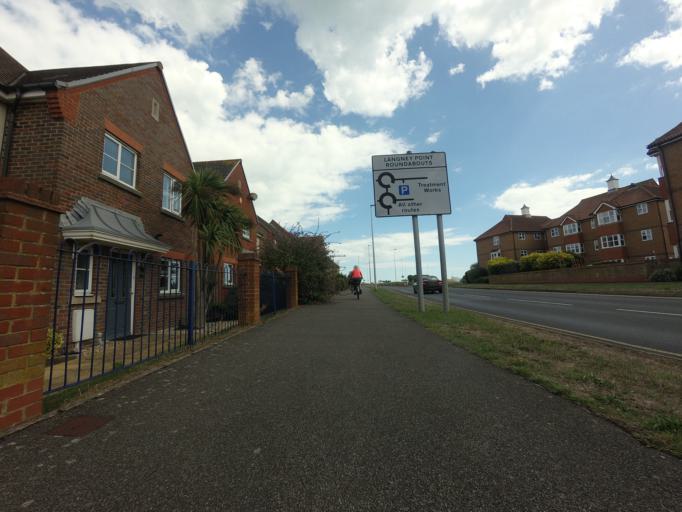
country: GB
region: England
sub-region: East Sussex
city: Pevensey
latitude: 50.7865
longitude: 0.3273
